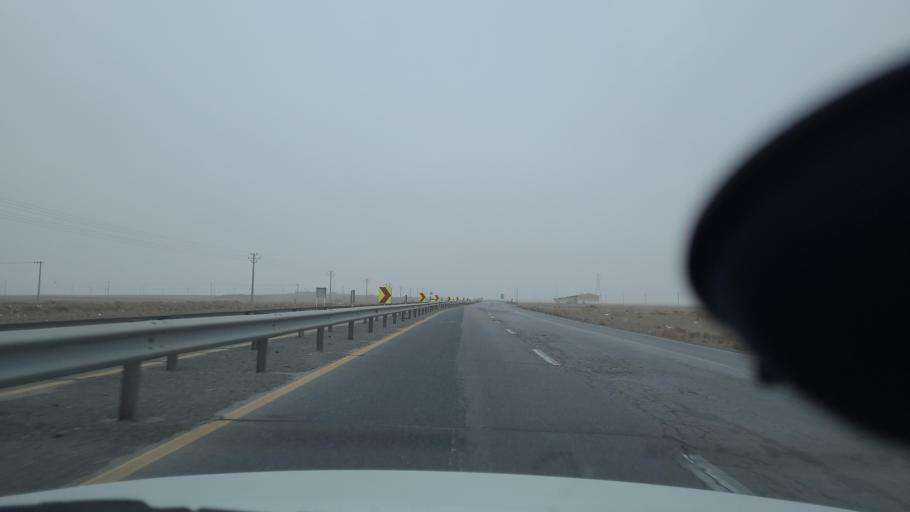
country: IR
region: Razavi Khorasan
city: Fariman
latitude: 35.9033
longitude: 59.7567
